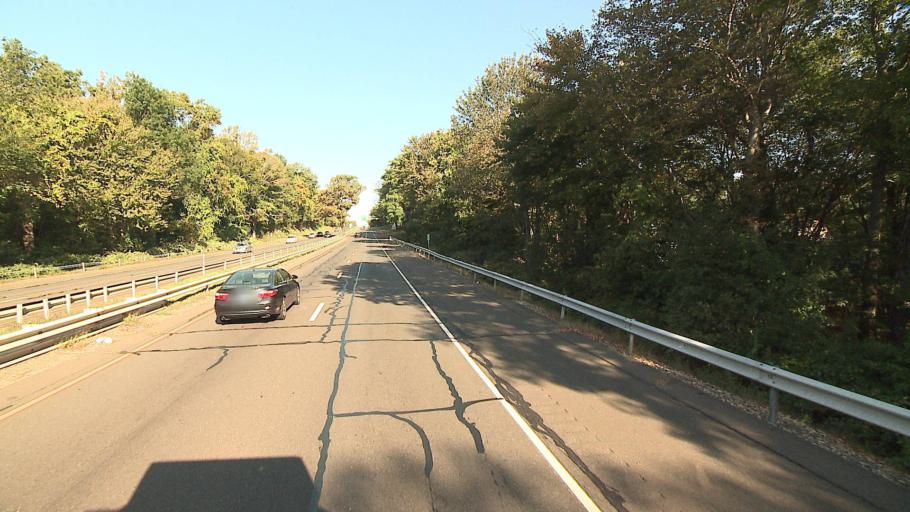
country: US
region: Connecticut
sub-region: New Haven County
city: City of Milford (balance)
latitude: 41.2368
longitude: -73.0744
